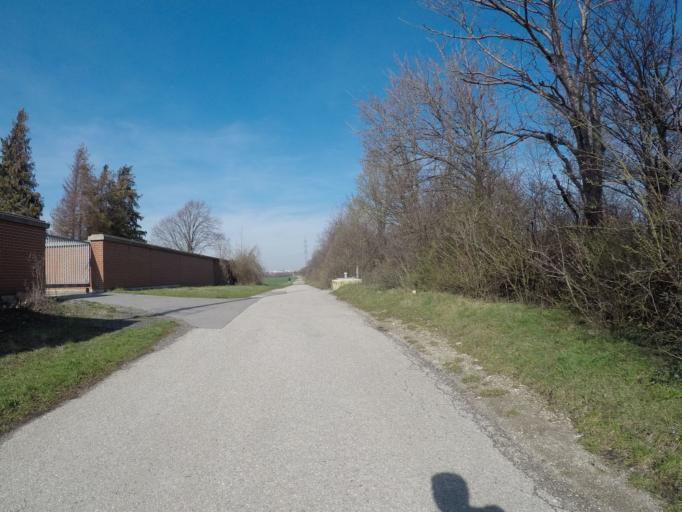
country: AT
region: Lower Austria
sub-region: Politischer Bezirk Modling
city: Vosendorf
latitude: 48.1260
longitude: 16.3431
